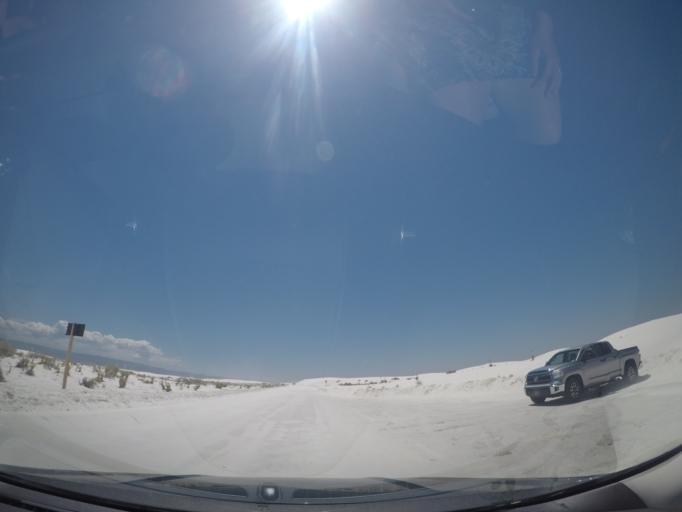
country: US
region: New Mexico
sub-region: Otero County
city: Holloman Air Force Base
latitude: 32.8019
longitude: -106.2568
